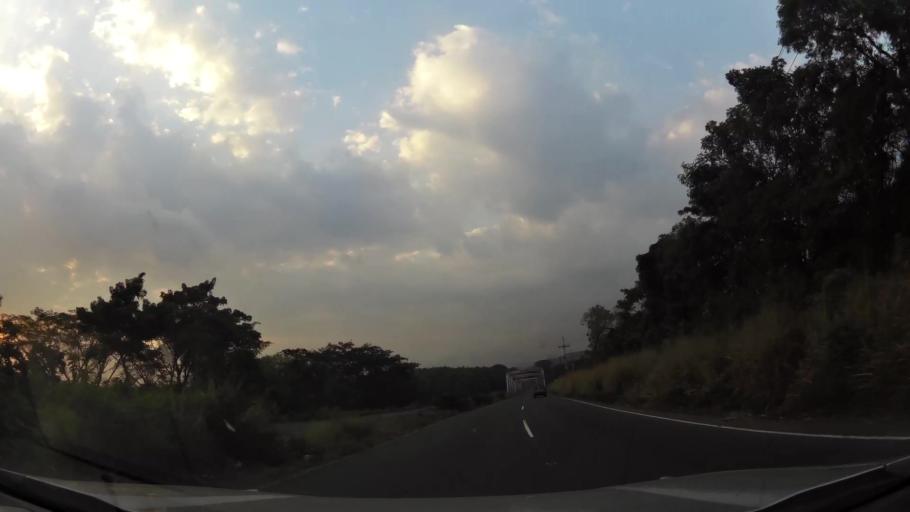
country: GT
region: Escuintla
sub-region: Municipio de La Democracia
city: La Democracia
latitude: 14.2669
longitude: -90.8959
